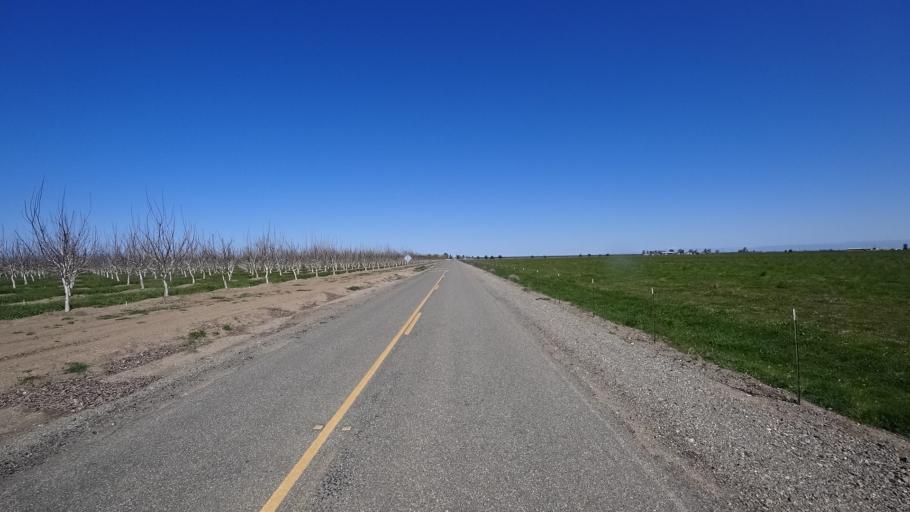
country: US
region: California
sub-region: Glenn County
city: Willows
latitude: 39.6256
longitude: -122.2535
